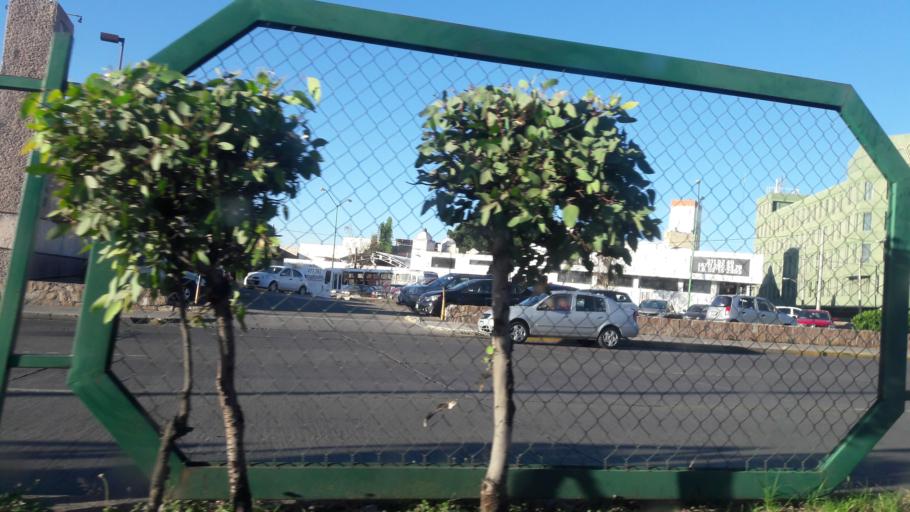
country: MX
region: Guanajuato
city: Leon
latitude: 21.1418
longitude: -101.6894
